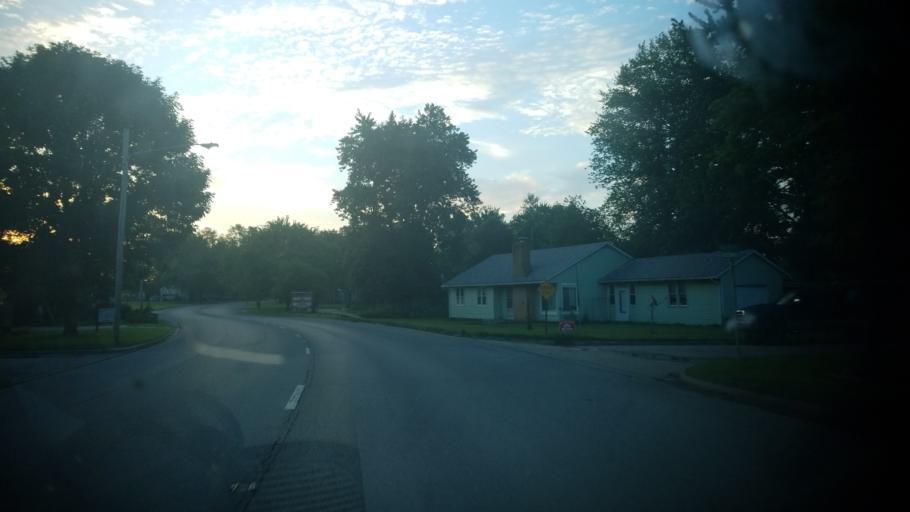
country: US
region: Illinois
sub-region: Wayne County
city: Fairfield
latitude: 38.3784
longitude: -88.3814
